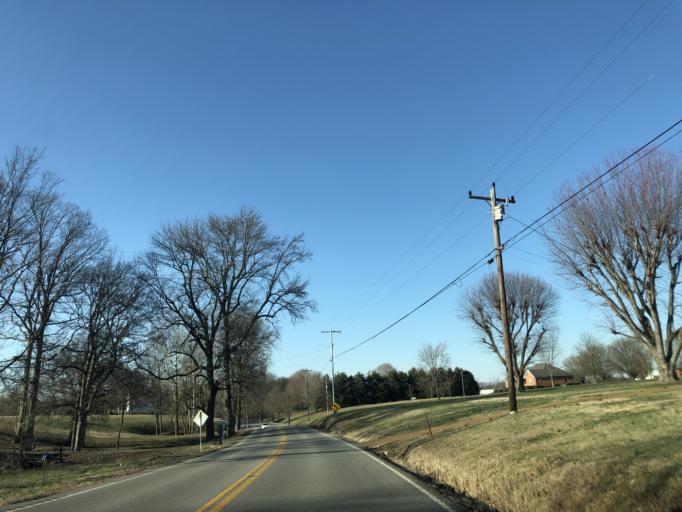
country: US
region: Tennessee
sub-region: Sumner County
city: White House
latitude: 36.4889
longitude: -86.5855
